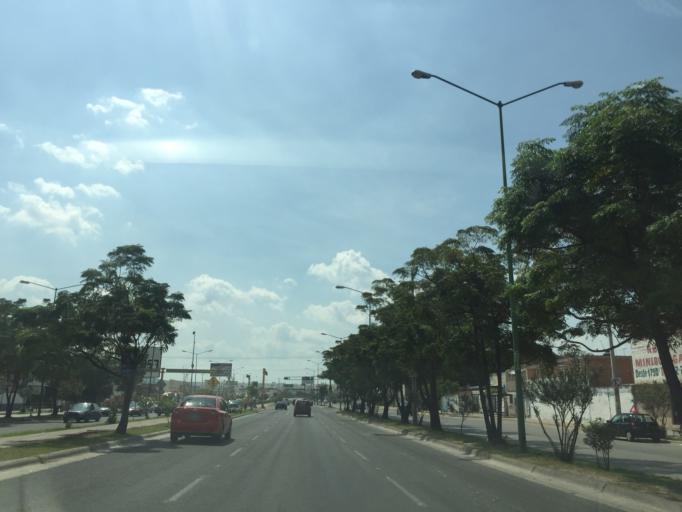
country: MX
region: Guanajuato
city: Leon
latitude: 21.1735
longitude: -101.6658
